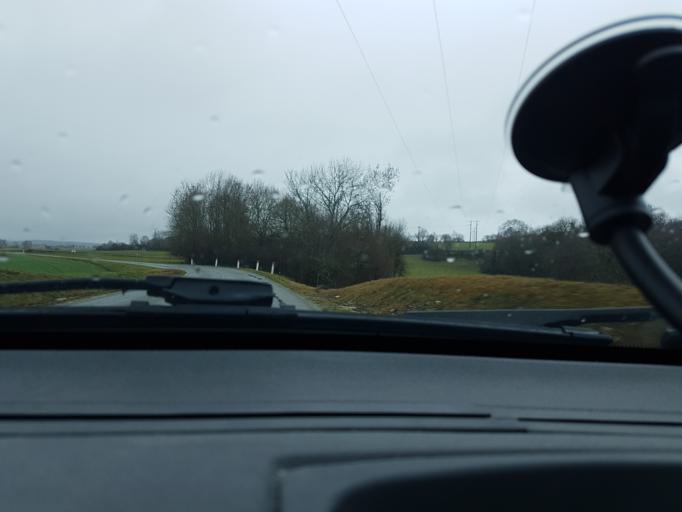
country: FR
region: Franche-Comte
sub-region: Departement du Doubs
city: Valdahon
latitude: 47.1053
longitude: 6.3584
